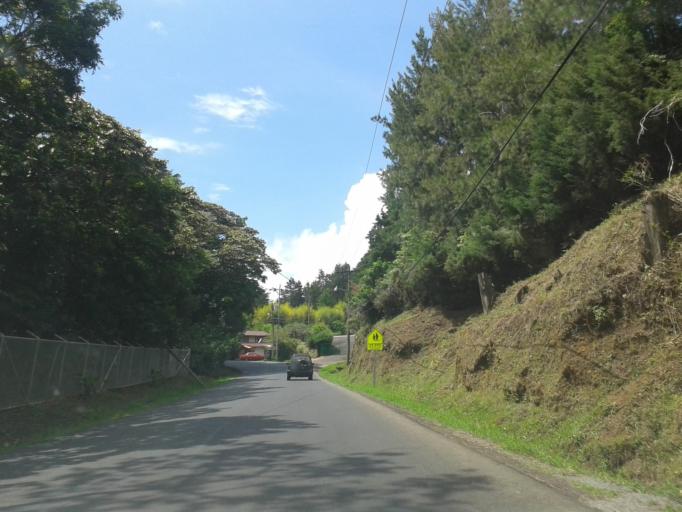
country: CR
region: Alajuela
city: Sabanilla
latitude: 10.1250
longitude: -84.1899
